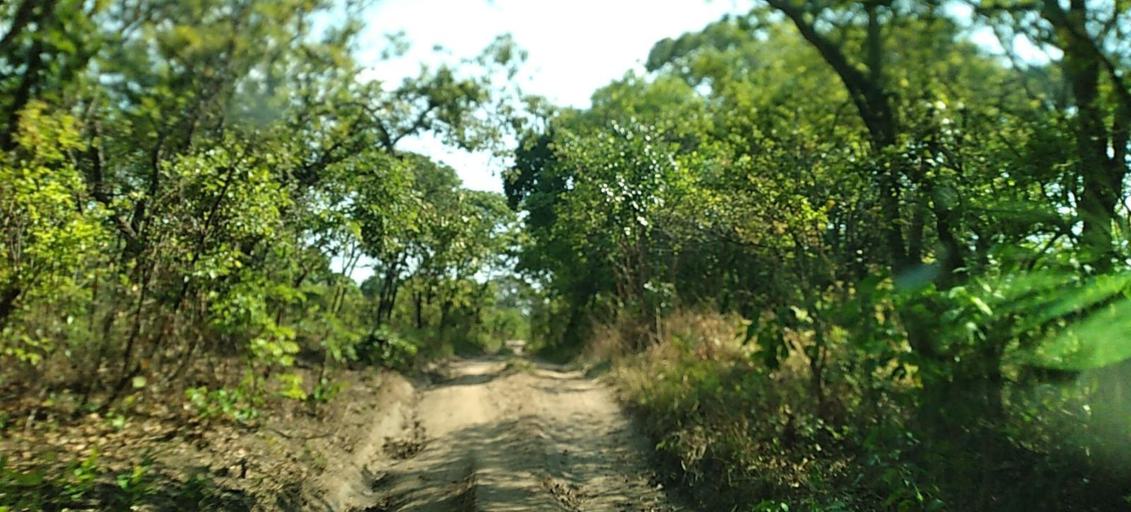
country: ZM
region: North-Western
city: Mwinilunga
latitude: -11.2804
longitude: 24.9255
